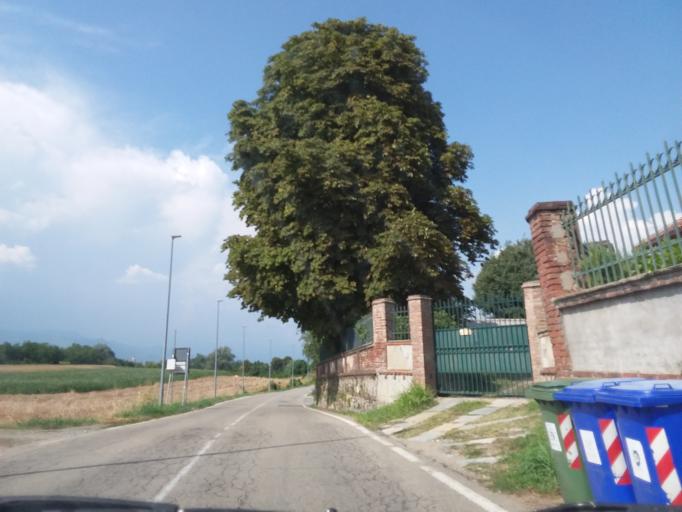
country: IT
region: Piedmont
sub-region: Provincia di Torino
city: Rivoli
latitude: 45.0779
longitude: 7.5424
